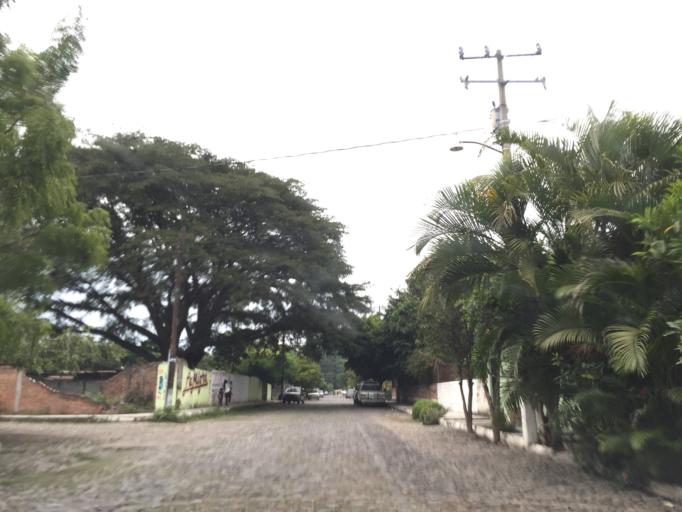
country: MX
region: Colima
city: Comala
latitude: 19.3690
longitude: -103.7993
